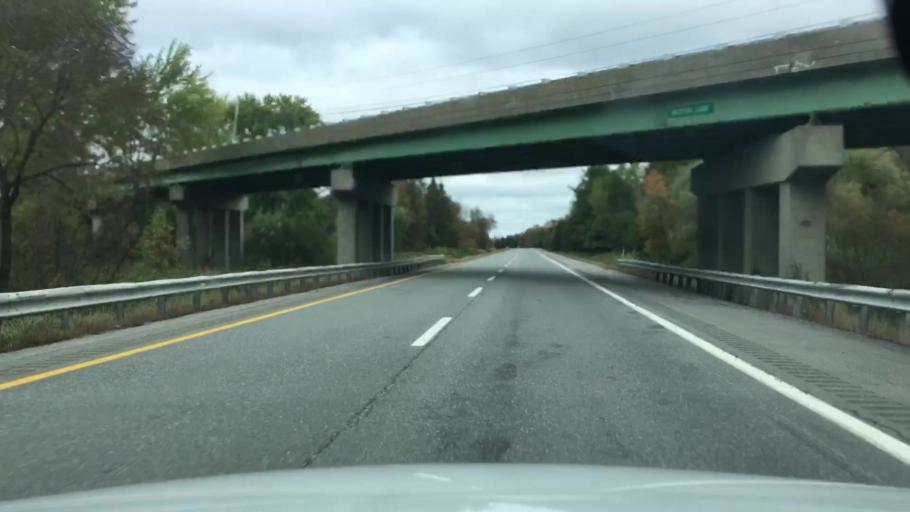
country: US
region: Maine
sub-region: Kennebec County
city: Clinton
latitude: 44.6610
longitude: -69.4985
